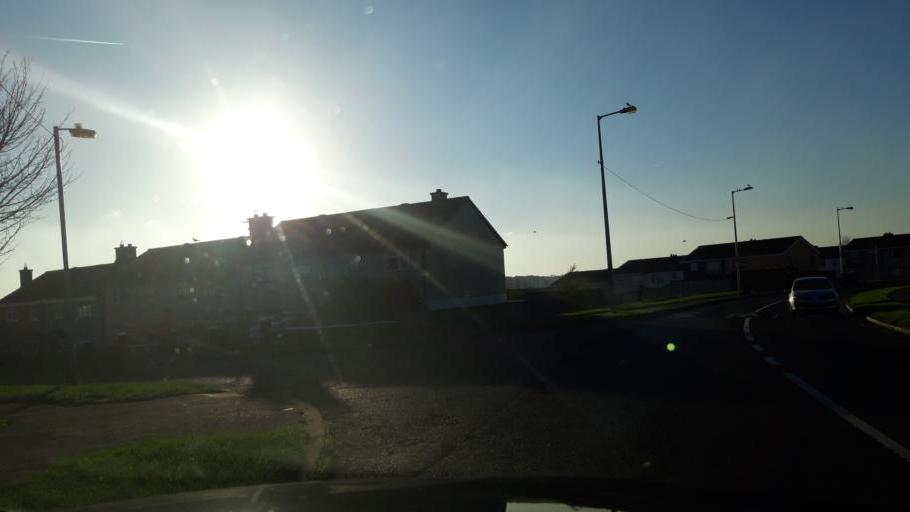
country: IE
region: Leinster
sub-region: Dublin City
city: Finglas
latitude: 53.3804
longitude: -6.3048
